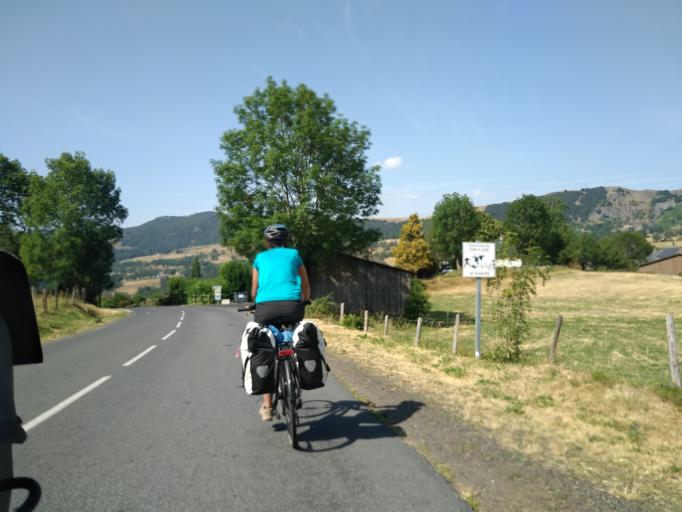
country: FR
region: Auvergne
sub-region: Departement du Cantal
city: Riom-es-Montagnes
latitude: 45.2124
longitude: 2.7185
